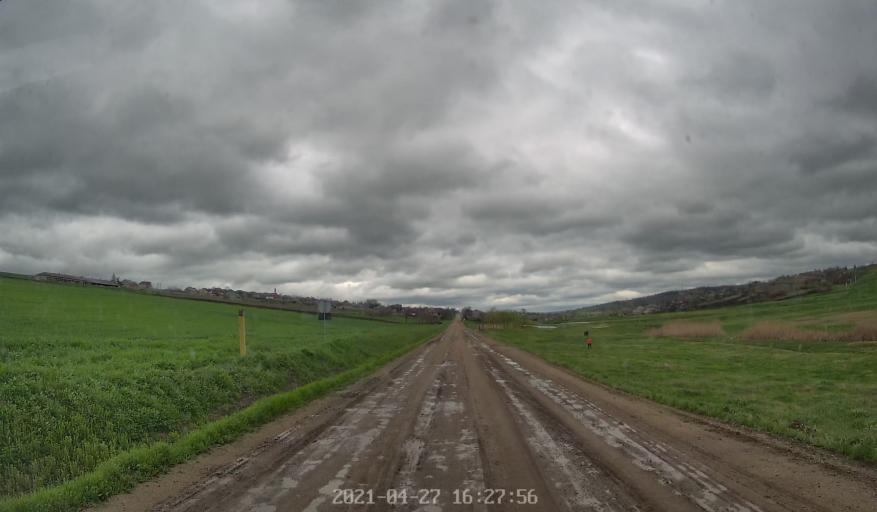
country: MD
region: Chisinau
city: Singera
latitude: 46.9737
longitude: 29.0378
